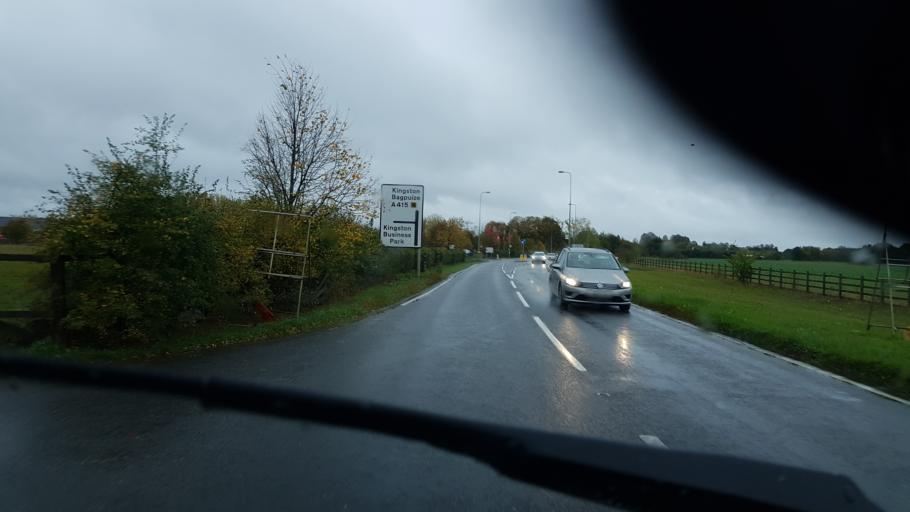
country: GB
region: England
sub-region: Oxfordshire
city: Frilford
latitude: 51.6766
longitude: -1.3995
